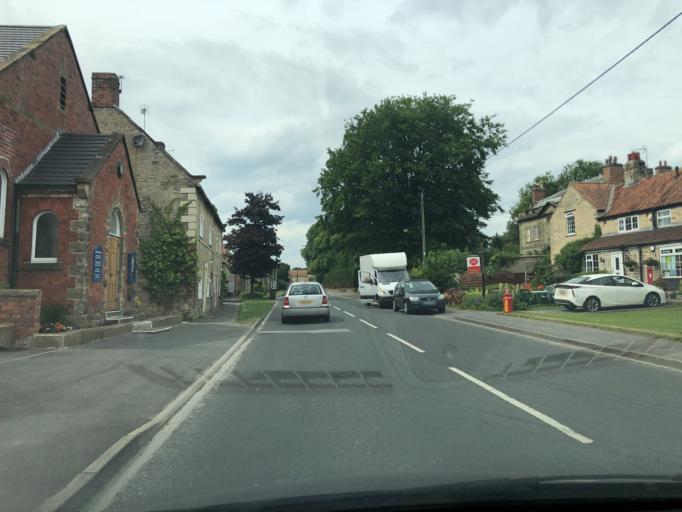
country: GB
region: England
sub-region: North Yorkshire
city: Pickering
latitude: 54.2572
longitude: -0.7996
